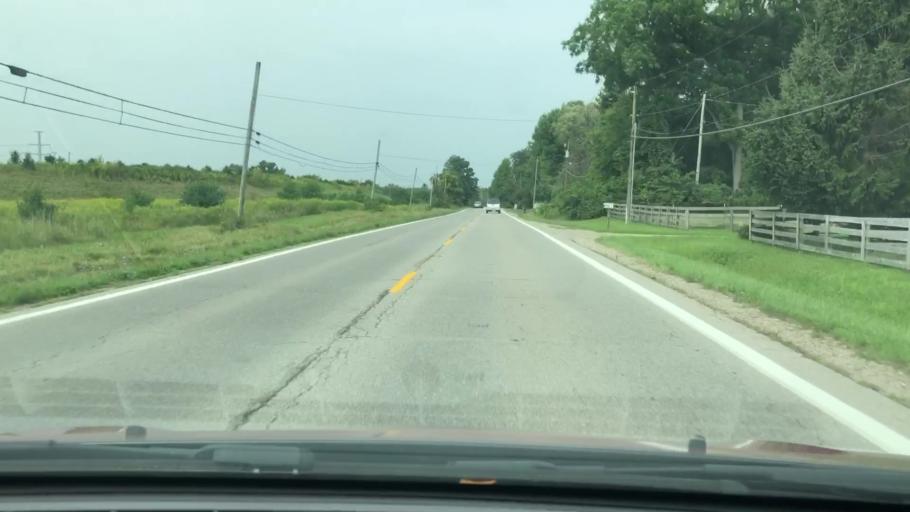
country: US
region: Ohio
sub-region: Delaware County
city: Sunbury
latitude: 40.2341
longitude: -82.8428
